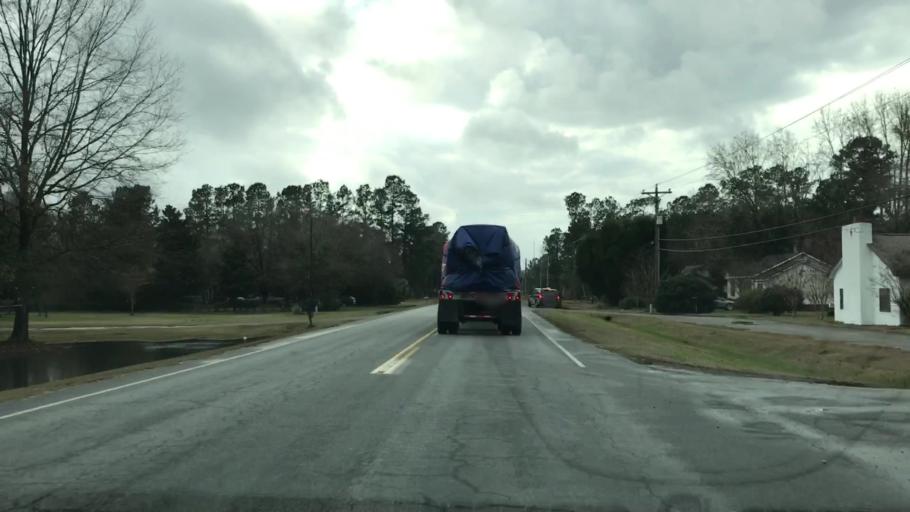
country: US
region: South Carolina
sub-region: Berkeley County
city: Bonneau Beach
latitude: 33.2759
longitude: -79.8906
